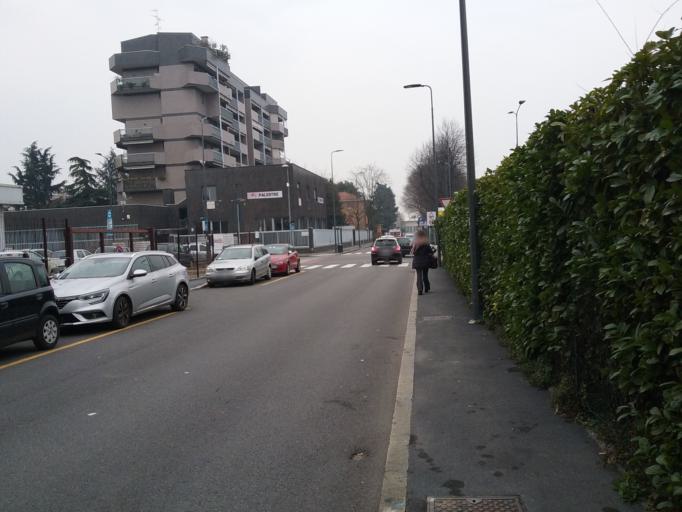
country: IT
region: Lombardy
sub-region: Citta metropolitana di Milano
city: Romano Banco
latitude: 45.4722
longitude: 9.1174
